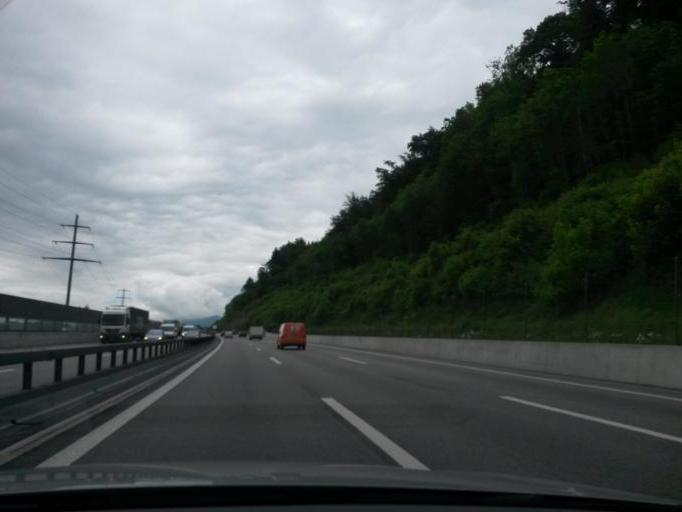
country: CH
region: Aargau
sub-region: Bezirk Zofingen
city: Rothrist
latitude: 47.3130
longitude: 7.8763
